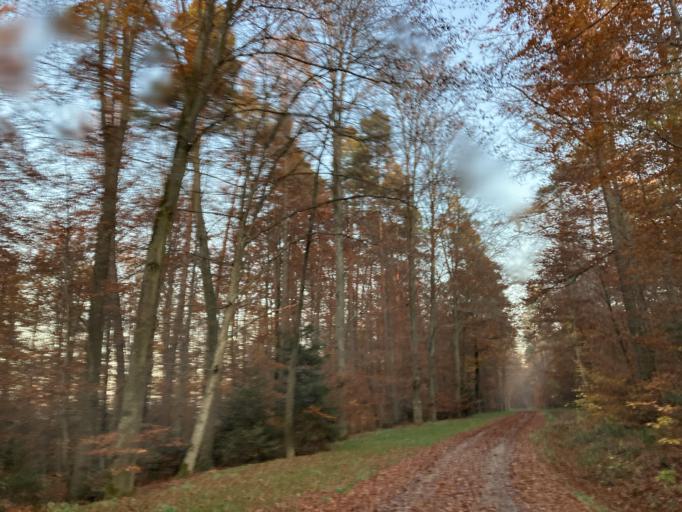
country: DE
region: Baden-Wuerttemberg
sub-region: Tuebingen Region
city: Dettenhausen
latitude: 48.5926
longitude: 9.0790
